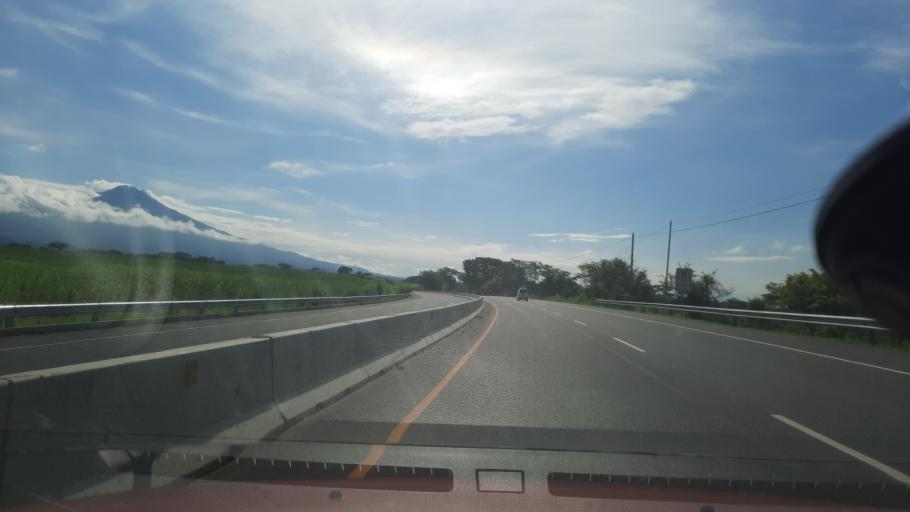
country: SV
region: La Paz
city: Santiago Nonualco
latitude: 13.4854
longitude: -88.9726
